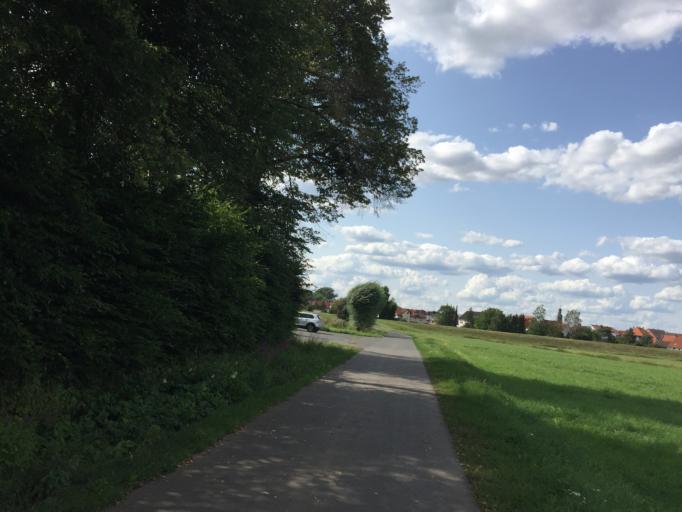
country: DE
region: Hesse
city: Schwalmstadt
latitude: 50.9094
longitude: 9.2477
